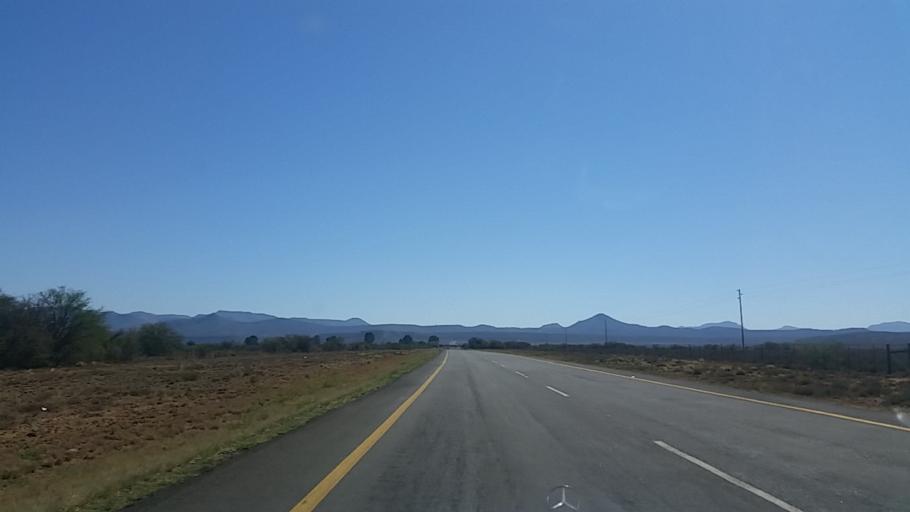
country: ZA
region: Eastern Cape
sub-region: Cacadu District Municipality
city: Graaff-Reinet
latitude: -32.2034
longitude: 24.5514
